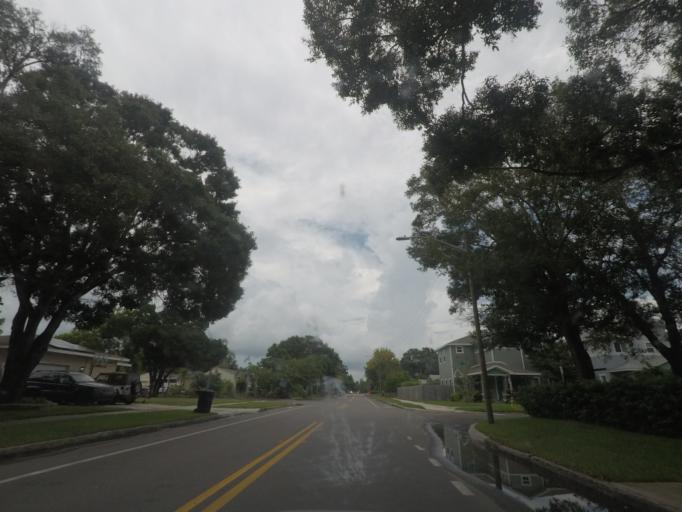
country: US
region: Florida
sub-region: Pinellas County
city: Lealman
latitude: 27.7993
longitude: -82.6493
